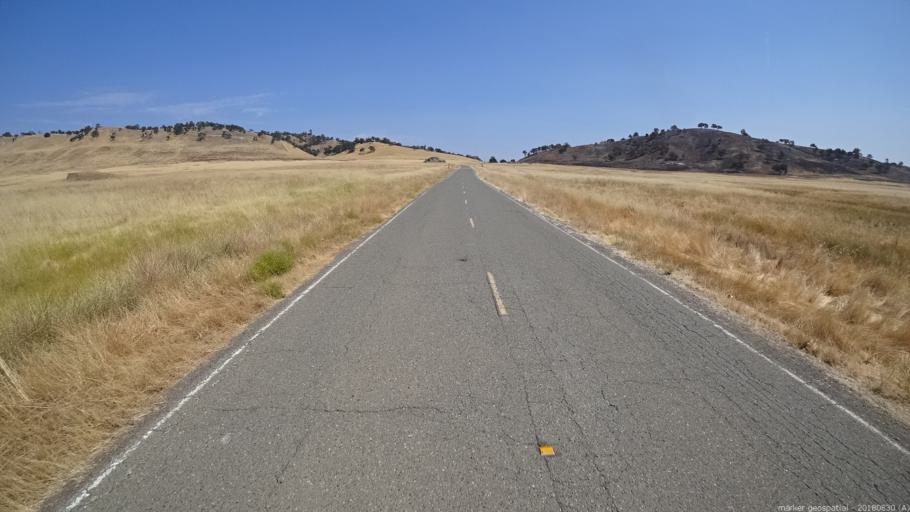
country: US
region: California
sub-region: Monterey County
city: King City
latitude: 35.9670
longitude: -121.2756
